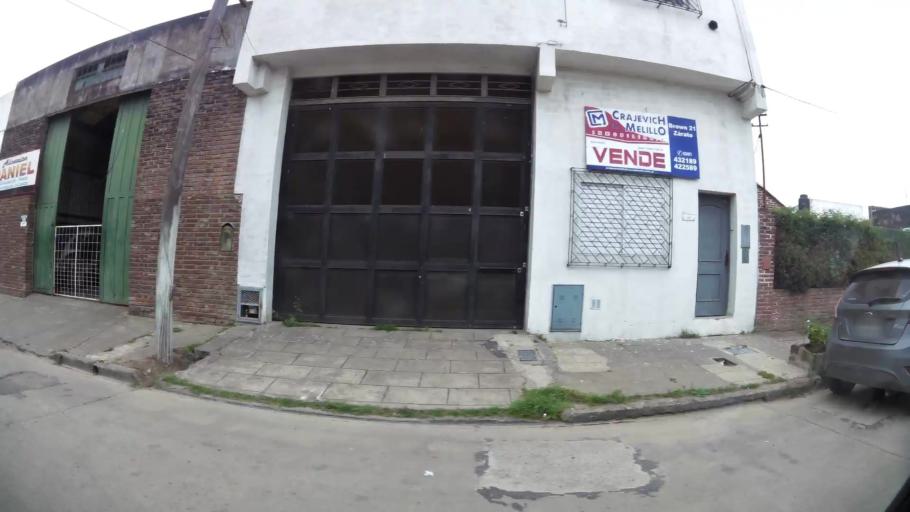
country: AR
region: Buenos Aires
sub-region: Partido de Zarate
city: Zarate
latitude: -34.1117
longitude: -59.0191
